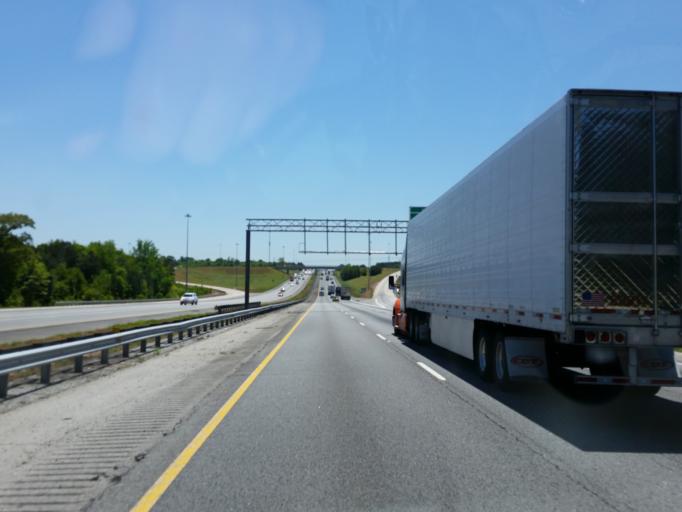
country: US
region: Georgia
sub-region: Henry County
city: Locust Grove
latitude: 33.2677
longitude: -84.0997
